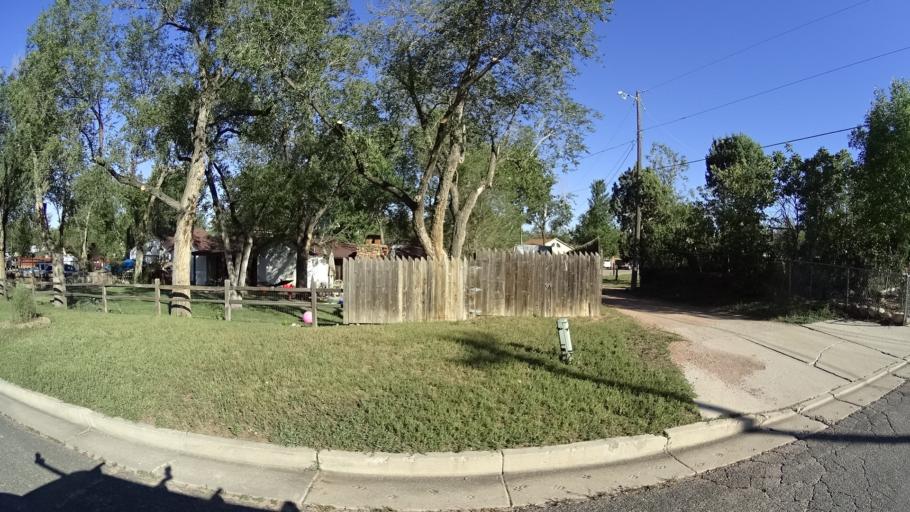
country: US
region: Colorado
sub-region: El Paso County
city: Colorado Springs
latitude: 38.8392
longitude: -104.8688
